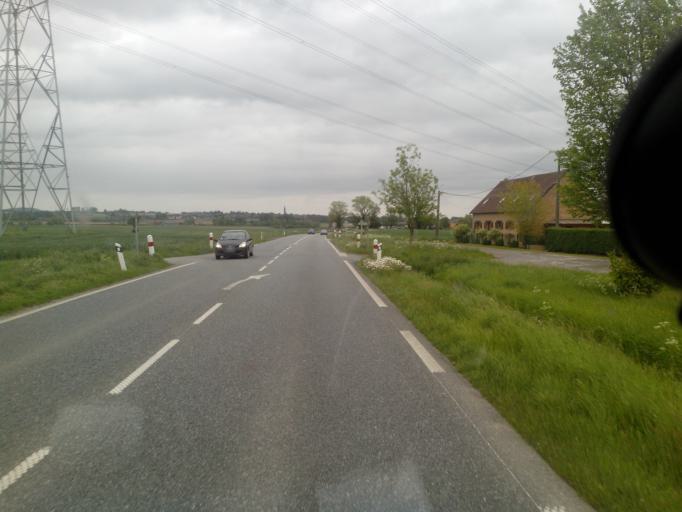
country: FR
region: Nord-Pas-de-Calais
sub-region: Departement du Nord
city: Vieux-Berquin
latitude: 50.7329
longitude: 2.6549
